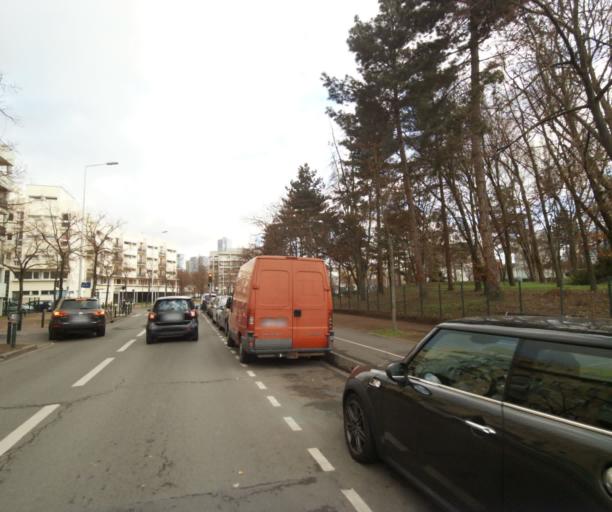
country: FR
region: Ile-de-France
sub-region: Departement des Hauts-de-Seine
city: Nanterre
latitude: 48.8903
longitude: 2.2181
